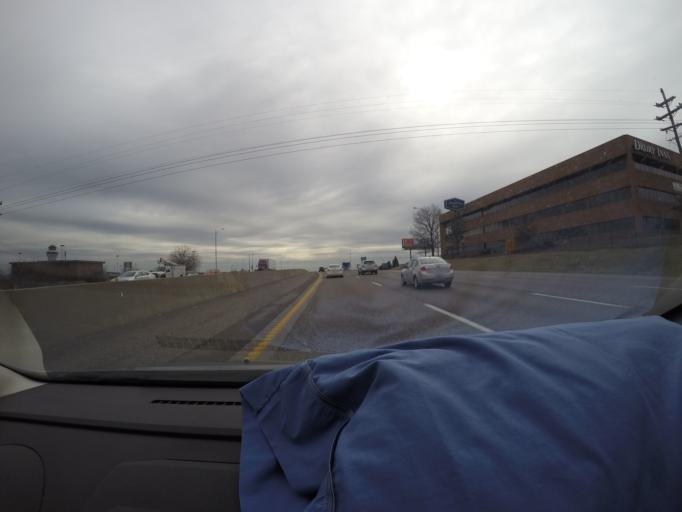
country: US
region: Missouri
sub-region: Saint Louis County
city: Saint Ann
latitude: 38.7399
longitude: -90.3713
